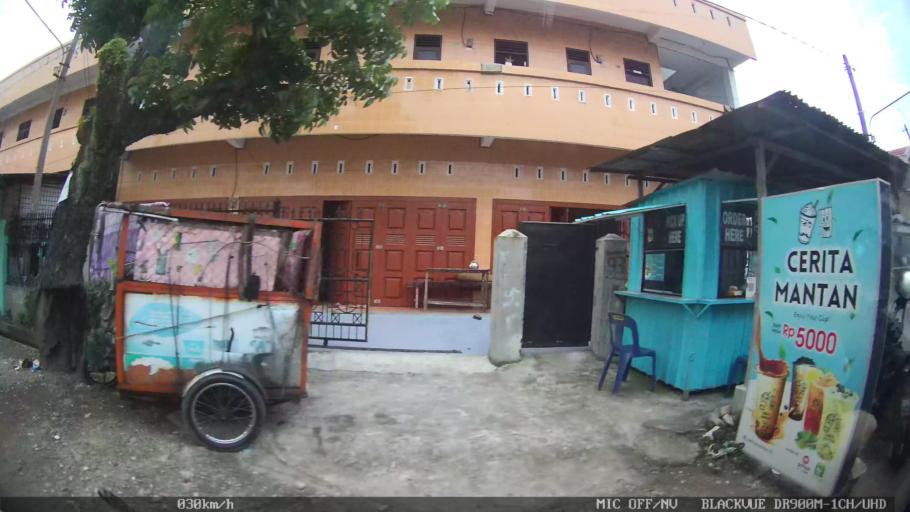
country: ID
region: North Sumatra
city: Medan
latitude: 3.6069
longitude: 98.7041
